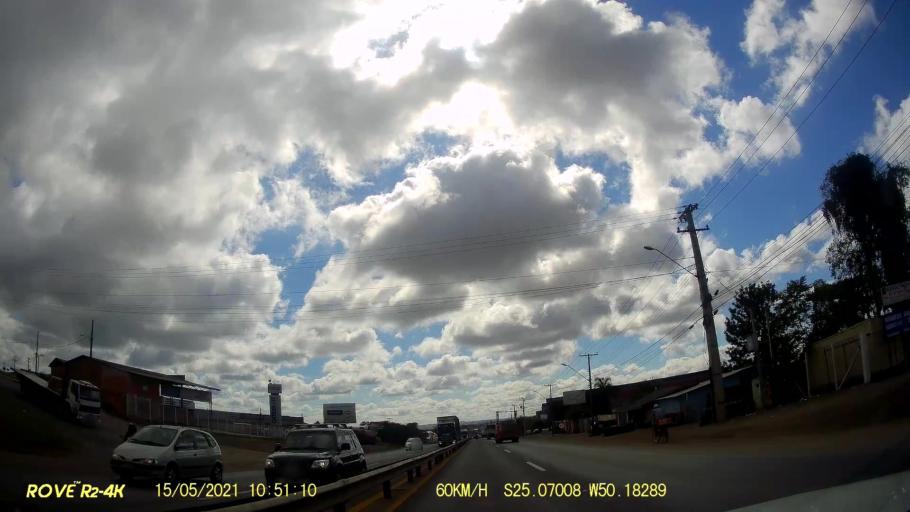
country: BR
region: Parana
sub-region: Ponta Grossa
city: Ponta Grossa
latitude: -25.0701
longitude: -50.1828
